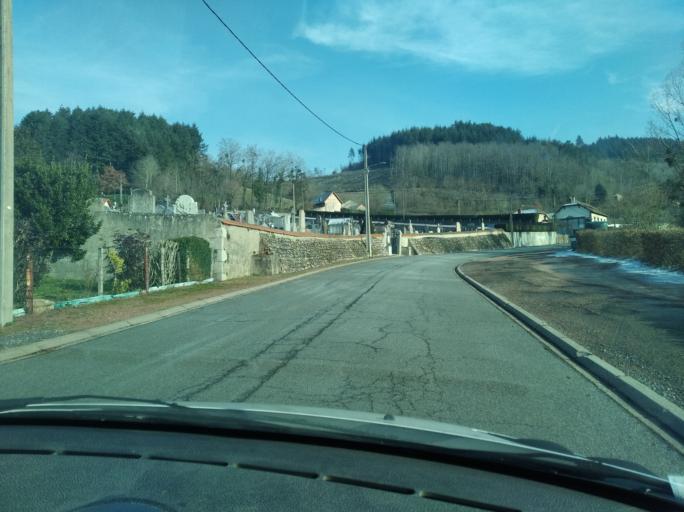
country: FR
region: Auvergne
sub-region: Departement de l'Allier
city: Le Mayet-de-Montagne
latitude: 46.1554
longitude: 3.7303
